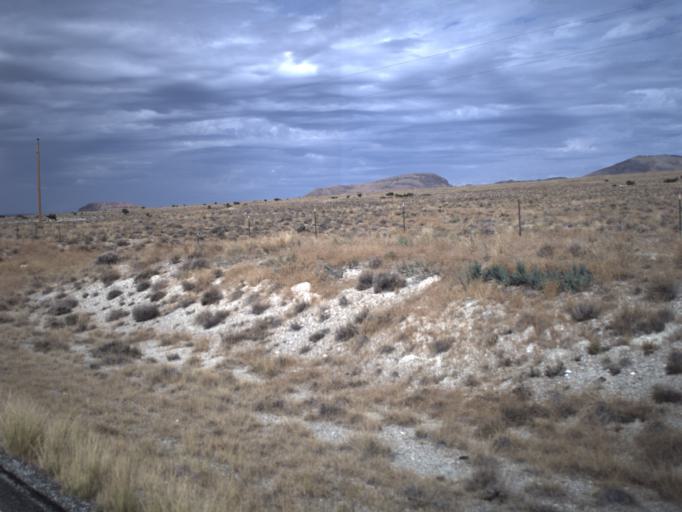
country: US
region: Utah
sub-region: Tooele County
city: Wendover
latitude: 41.4386
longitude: -113.7268
